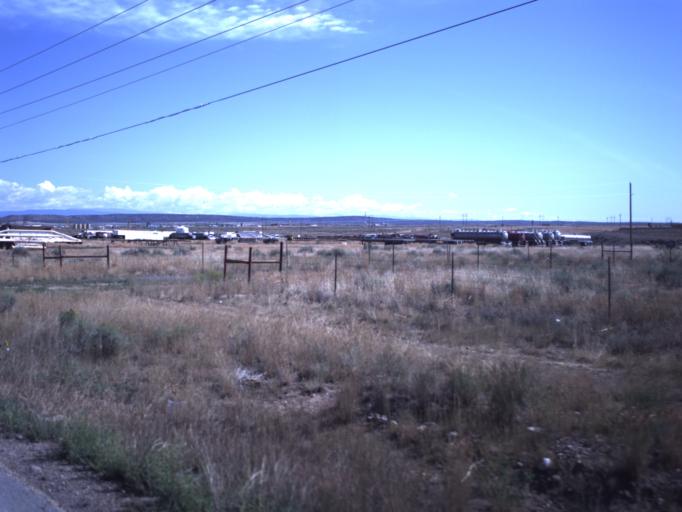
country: US
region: Utah
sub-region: Duchesne County
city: Duchesne
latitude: 40.2073
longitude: -110.3892
